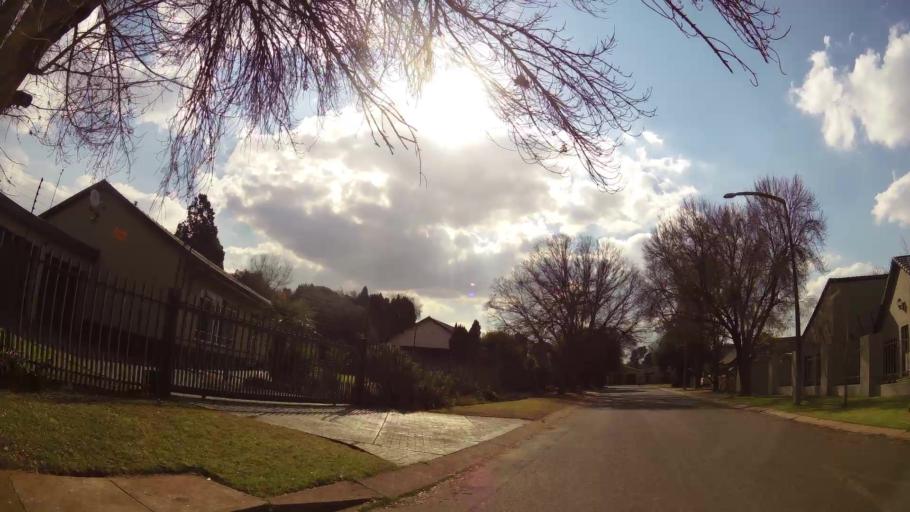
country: ZA
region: Mpumalanga
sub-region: Nkangala District Municipality
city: Delmas
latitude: -26.1423
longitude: 28.6736
